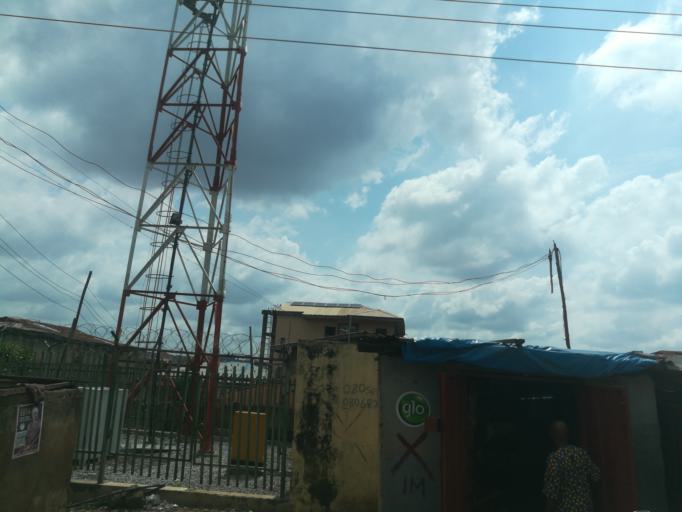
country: NG
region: Oyo
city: Ibadan
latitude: 7.3853
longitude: 3.9043
